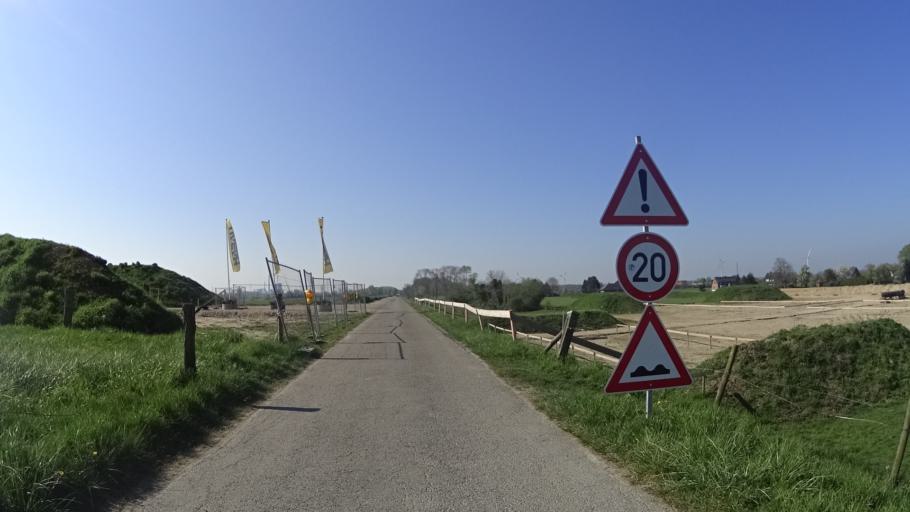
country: DE
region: North Rhine-Westphalia
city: Rheinberg
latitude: 51.5900
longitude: 6.5837
